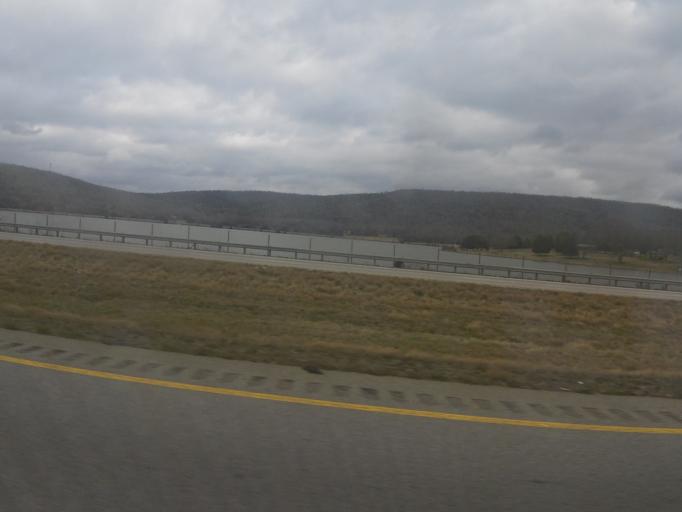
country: US
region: Tennessee
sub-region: Marion County
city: Jasper
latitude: 35.0277
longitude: -85.5667
